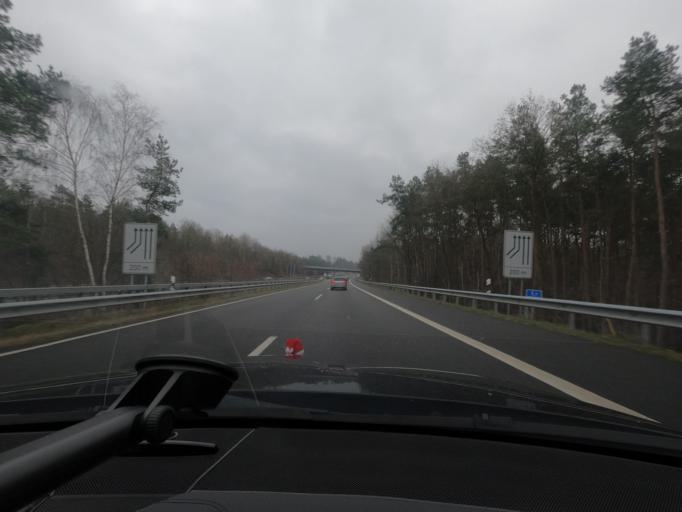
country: DE
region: Lower Saxony
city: Harmstorf
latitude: 53.3718
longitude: 10.0238
